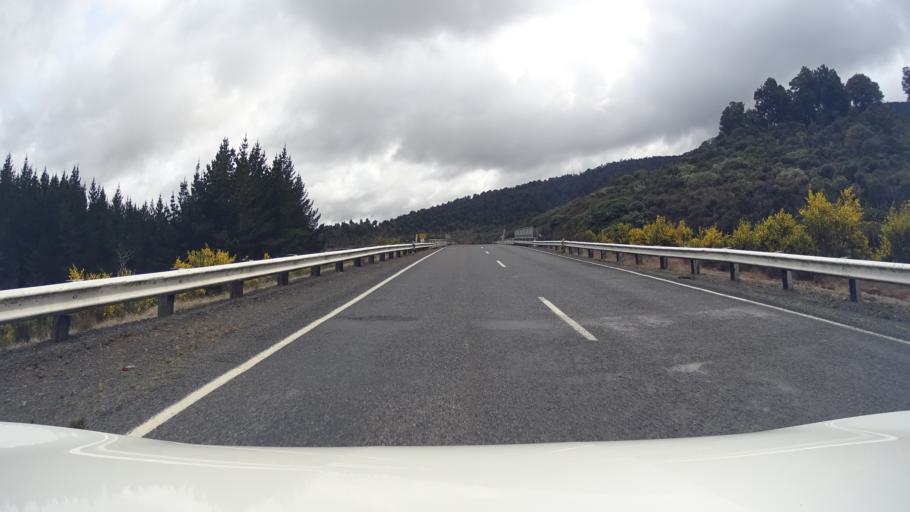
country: NZ
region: Manawatu-Wanganui
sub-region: Ruapehu District
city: Waiouru
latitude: -39.2231
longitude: 175.3982
